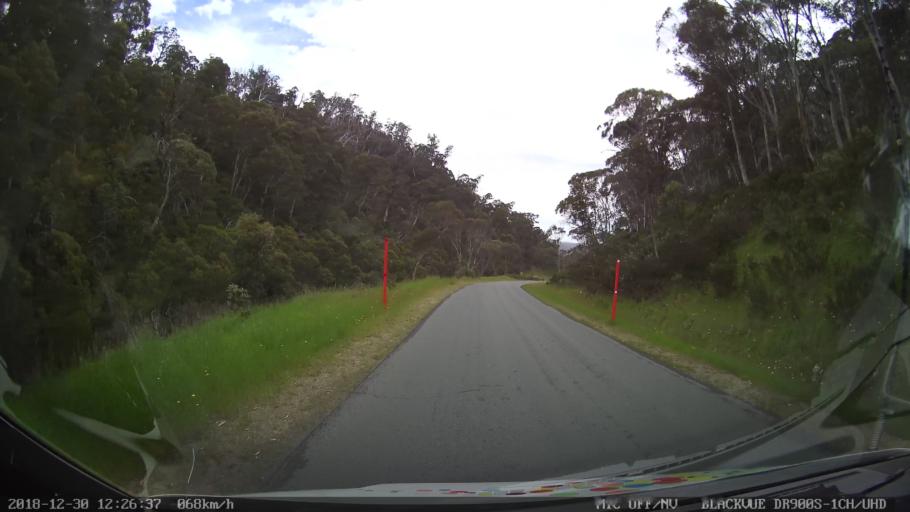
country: AU
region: New South Wales
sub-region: Snowy River
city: Jindabyne
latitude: -36.3372
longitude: 148.4894
